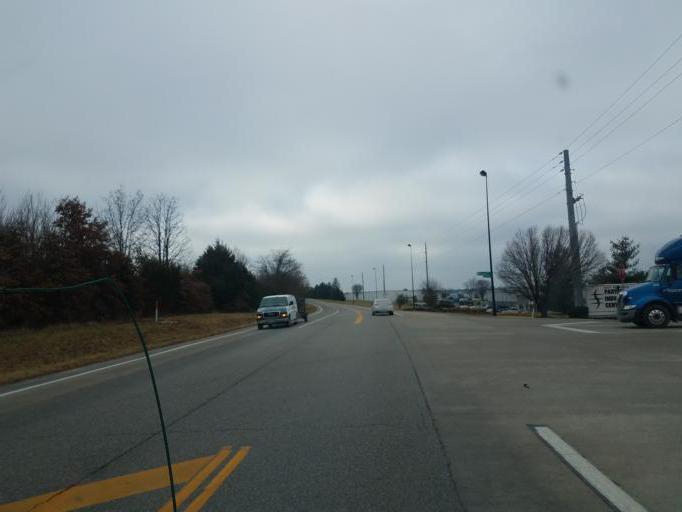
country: US
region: Missouri
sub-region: Greene County
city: Strafford
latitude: 37.2450
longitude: -93.1938
